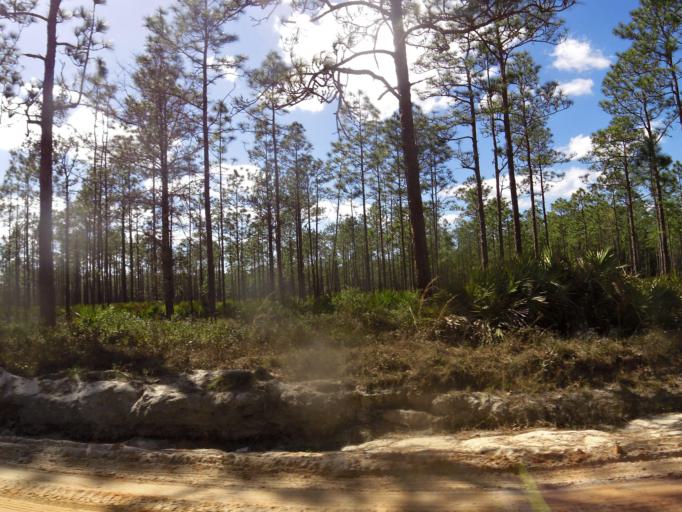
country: US
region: Florida
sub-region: Clay County
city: Middleburg
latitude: 30.1307
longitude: -81.9658
